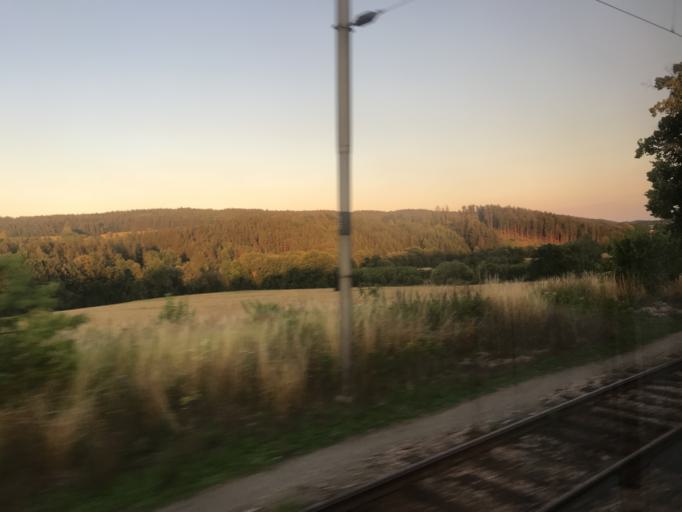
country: CZ
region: Central Bohemia
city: Votice
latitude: 49.6018
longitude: 14.5841
